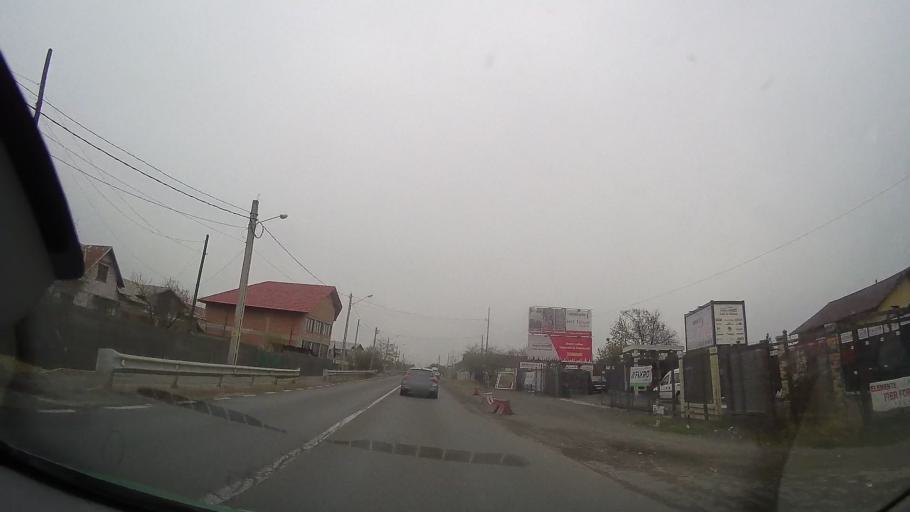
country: RO
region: Prahova
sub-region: Comuna Blejoiu
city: Ploiestiori
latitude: 44.9694
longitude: 26.0252
